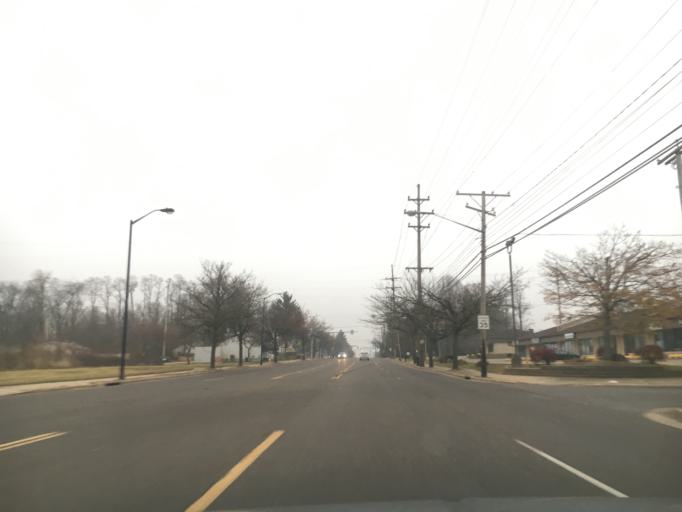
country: US
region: Ohio
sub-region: Summit County
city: Cuyahoga Falls
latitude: 41.1137
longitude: -81.4859
